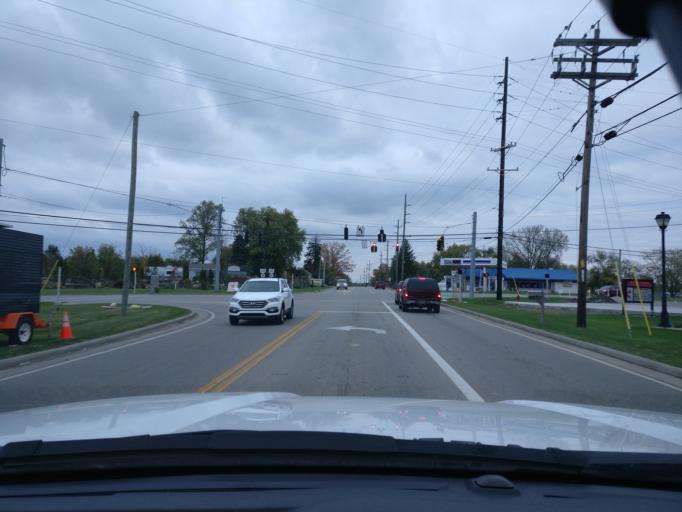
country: US
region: Ohio
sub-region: Warren County
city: Hunter
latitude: 39.4907
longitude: -84.2500
